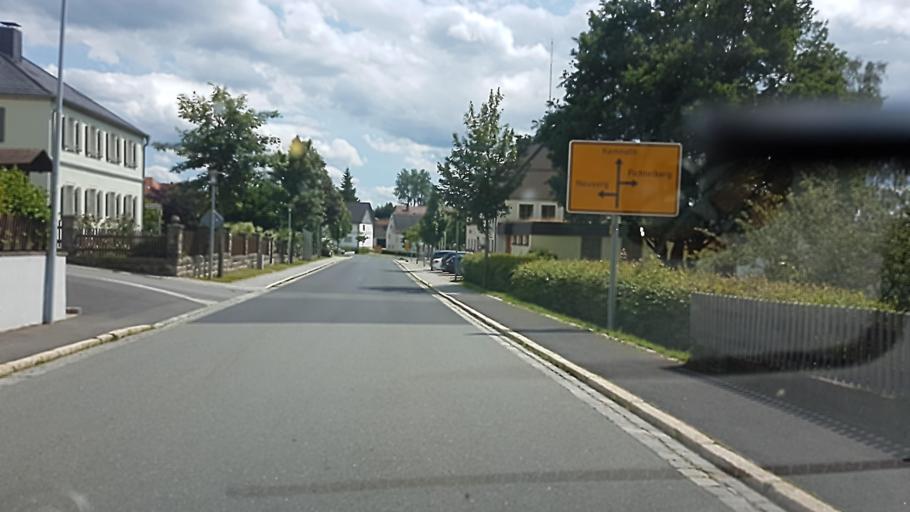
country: DE
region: Bavaria
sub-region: Upper Palatinate
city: Brand
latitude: 49.9605
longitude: 11.9077
